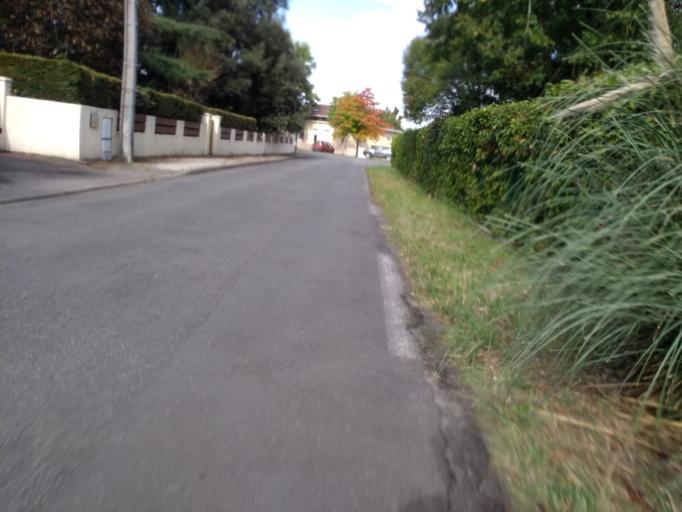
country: FR
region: Aquitaine
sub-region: Departement de la Gironde
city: Gradignan
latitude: 44.7799
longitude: -0.6224
